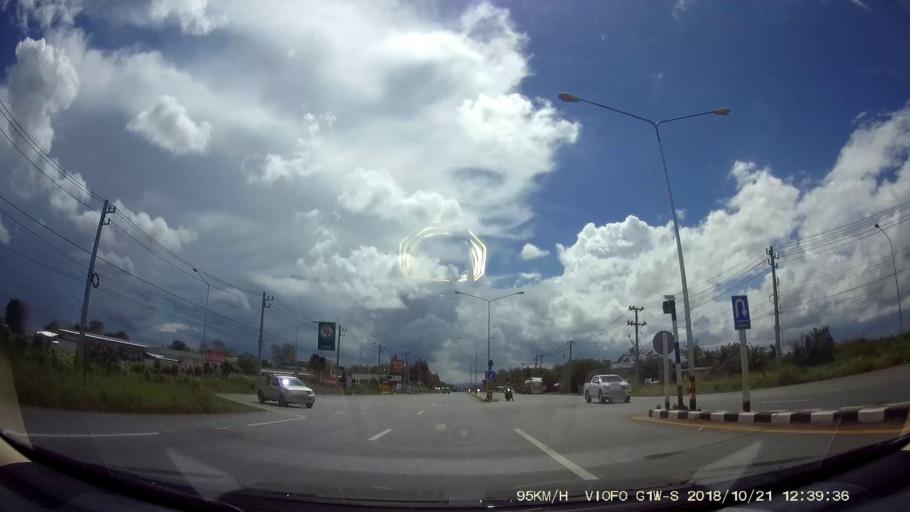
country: TH
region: Nakhon Ratchasima
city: Amphoe Sikhiu
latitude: 15.0370
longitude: 101.7000
